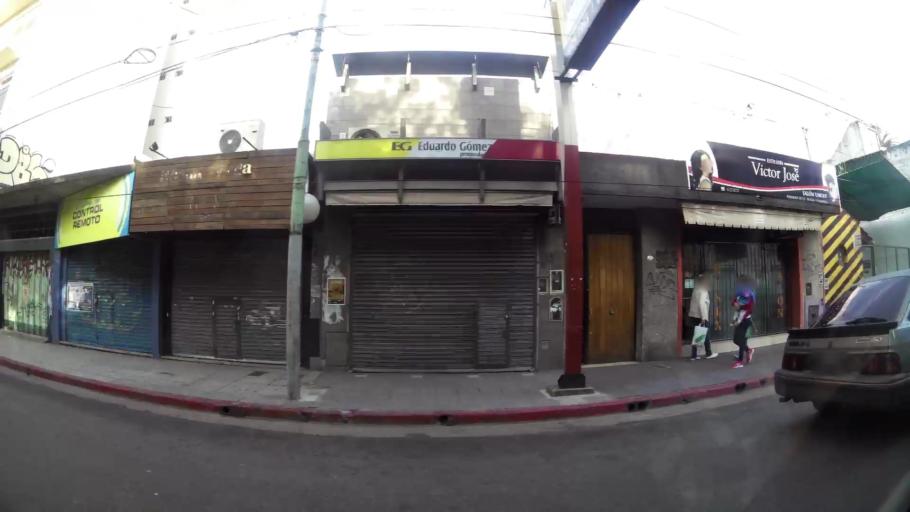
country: AR
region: Buenos Aires
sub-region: Partido de Moron
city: Moron
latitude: -34.6512
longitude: -58.6186
